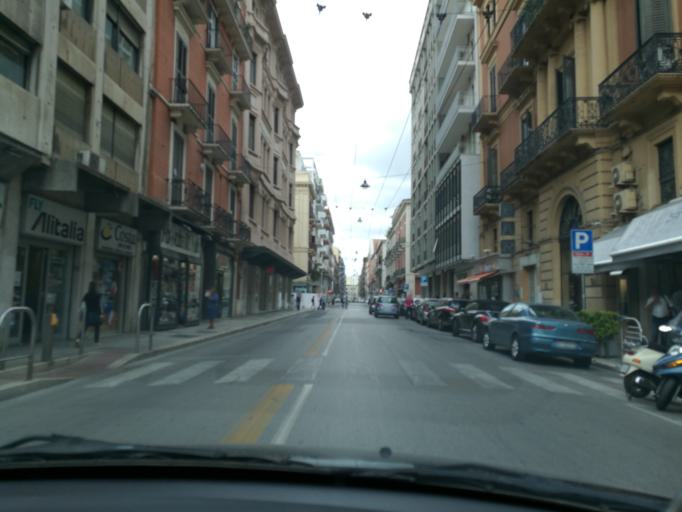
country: IT
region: Apulia
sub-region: Provincia di Bari
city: Bari
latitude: 41.1254
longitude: 16.8702
